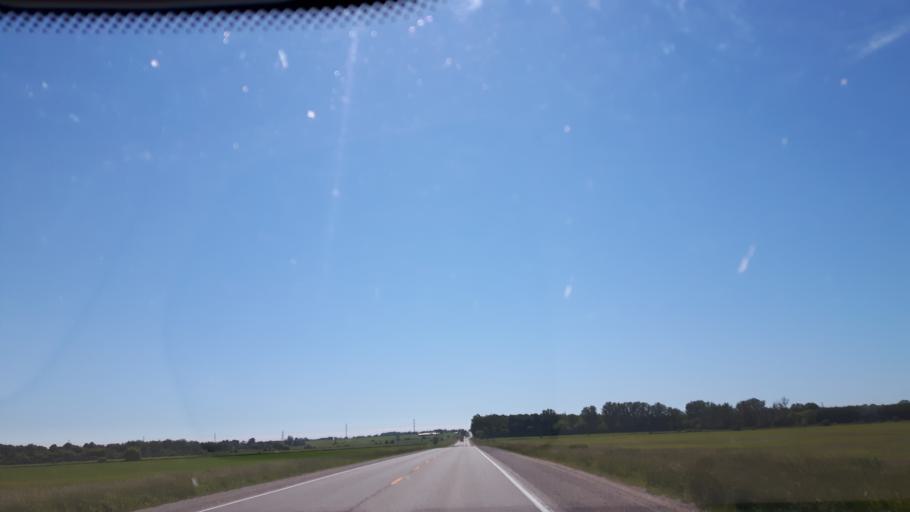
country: CA
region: Ontario
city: Bluewater
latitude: 43.4262
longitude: -81.5759
